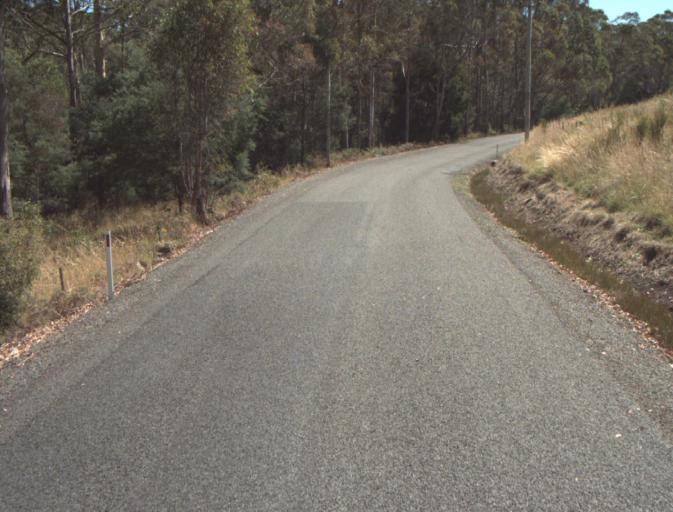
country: AU
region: Tasmania
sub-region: Launceston
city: Newstead
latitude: -41.3607
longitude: 147.3021
